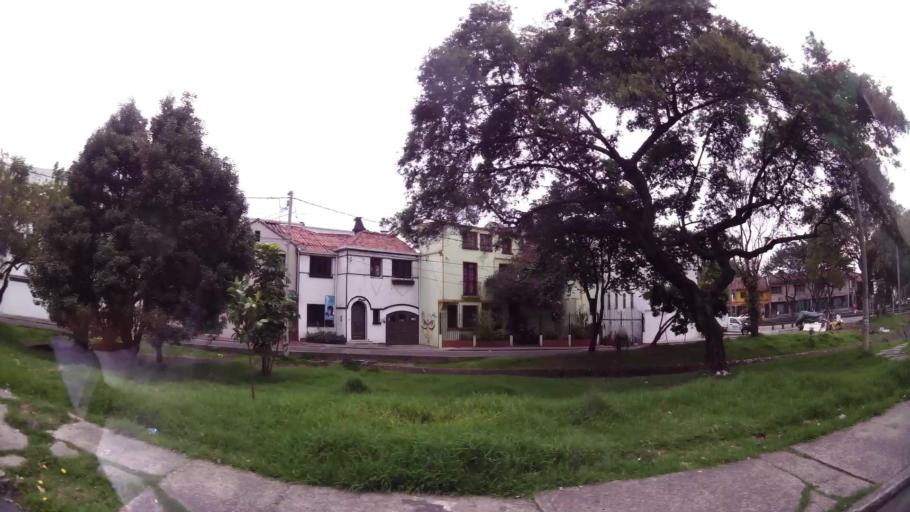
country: CO
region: Bogota D.C.
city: Bogota
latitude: 4.6283
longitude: -74.0678
